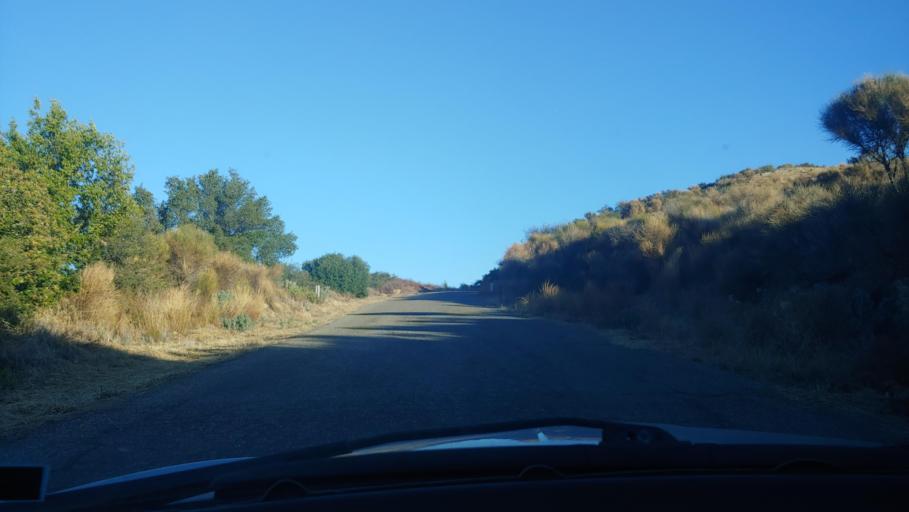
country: US
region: California
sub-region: Santa Barbara County
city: Mission Canyon
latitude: 34.5124
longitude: -119.7756
